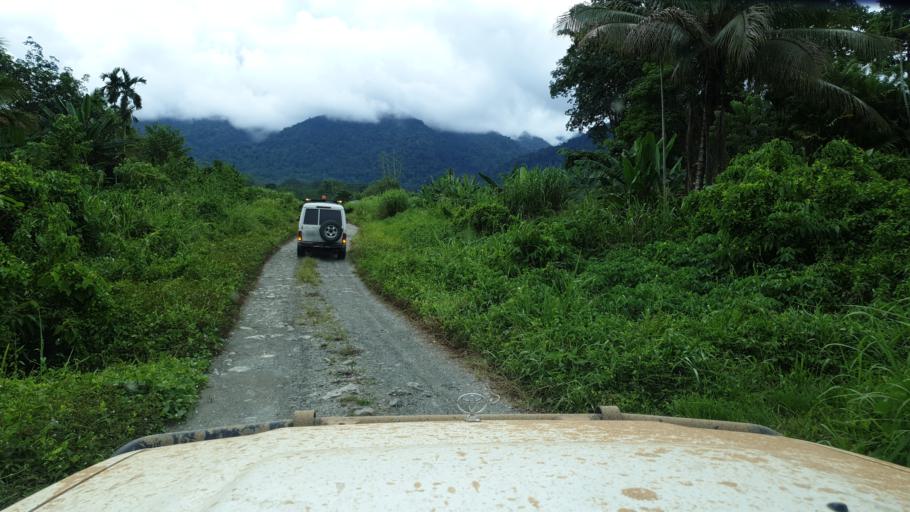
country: PG
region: Northern Province
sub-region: Sohe
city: Kokoda
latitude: -8.9389
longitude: 147.8677
